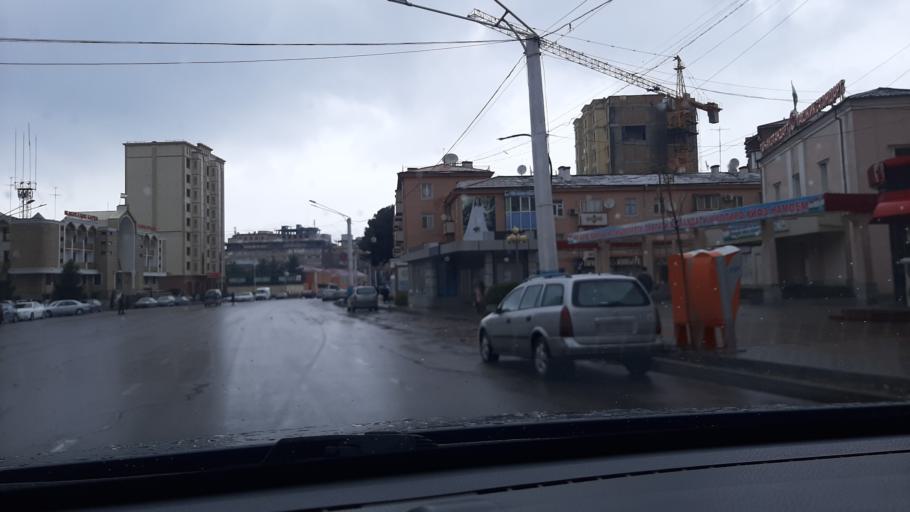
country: TJ
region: Viloyati Sughd
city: Khujand
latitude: 40.2796
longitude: 69.6272
